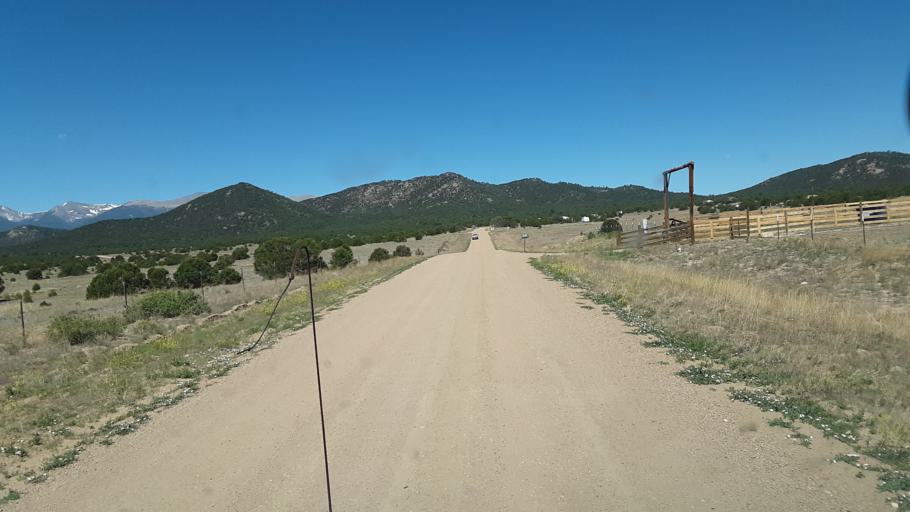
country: US
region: Colorado
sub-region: Custer County
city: Westcliffe
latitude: 38.2851
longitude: -105.5178
